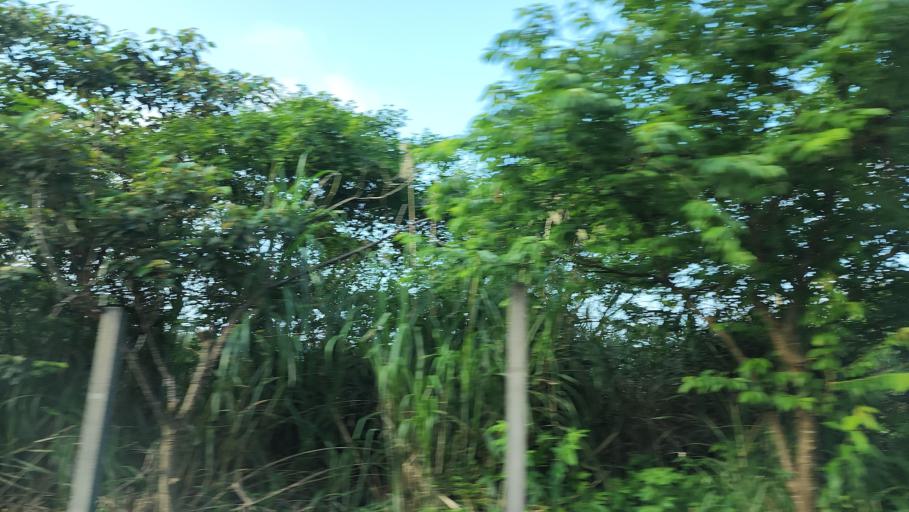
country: TW
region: Taiwan
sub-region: Keelung
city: Keelung
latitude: 25.1808
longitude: 121.6436
